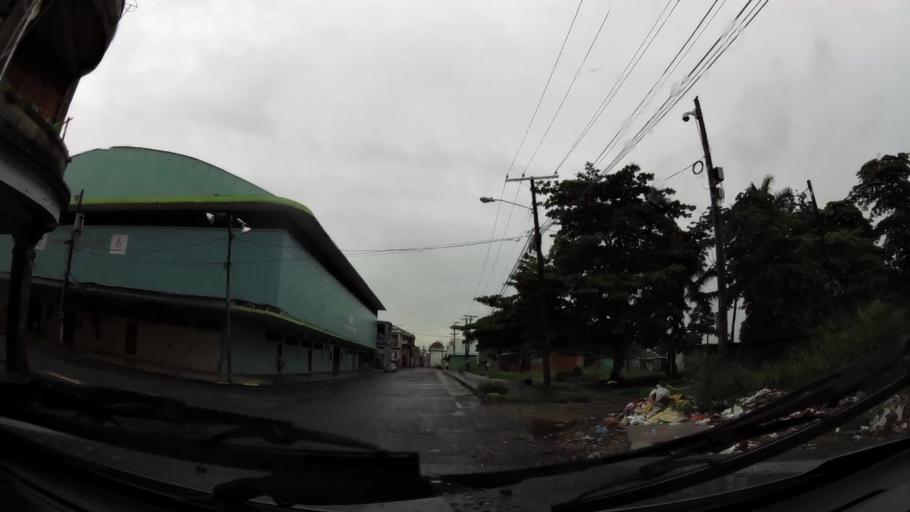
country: PA
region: Colon
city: Colon
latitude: 9.3598
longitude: -79.9055
